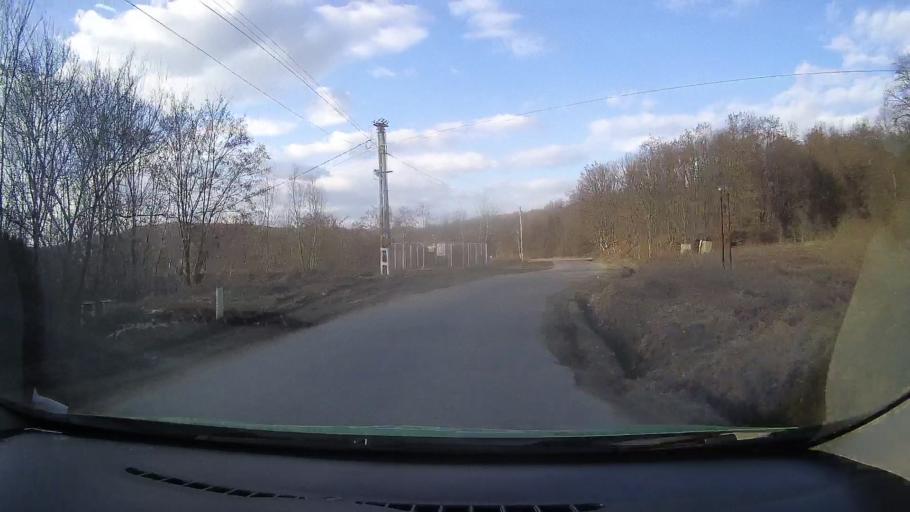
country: RO
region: Dambovita
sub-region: Comuna Ocnita
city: Ocnita
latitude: 44.9673
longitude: 25.5483
